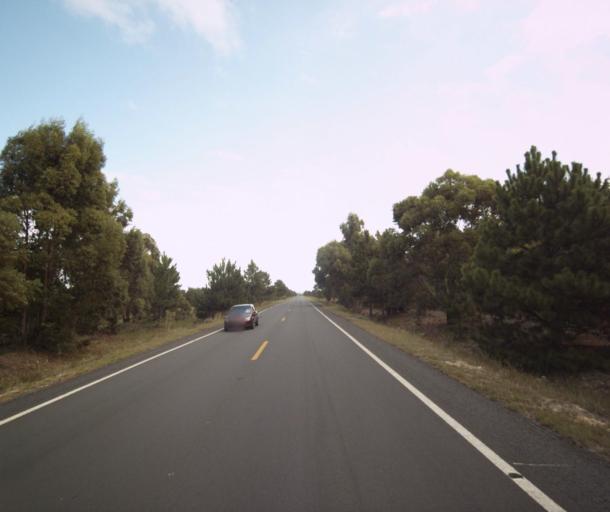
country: BR
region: Rio Grande do Sul
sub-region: Tapes
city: Tapes
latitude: -31.4308
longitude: -51.1892
